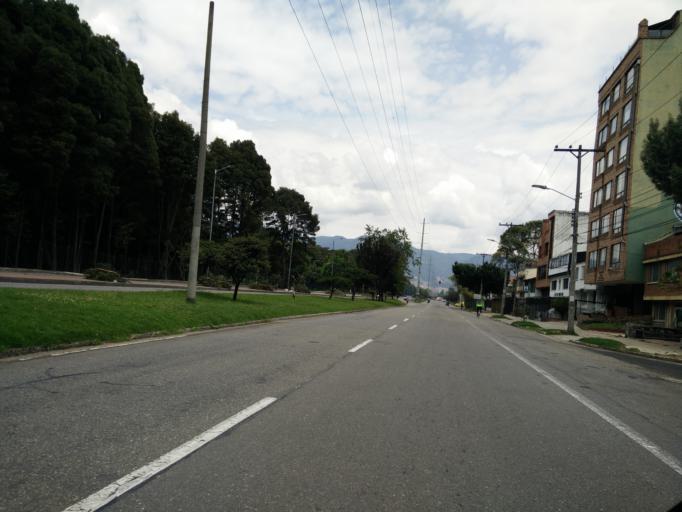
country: CO
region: Bogota D.C.
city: Bogota
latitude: 4.6558
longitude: -74.0987
